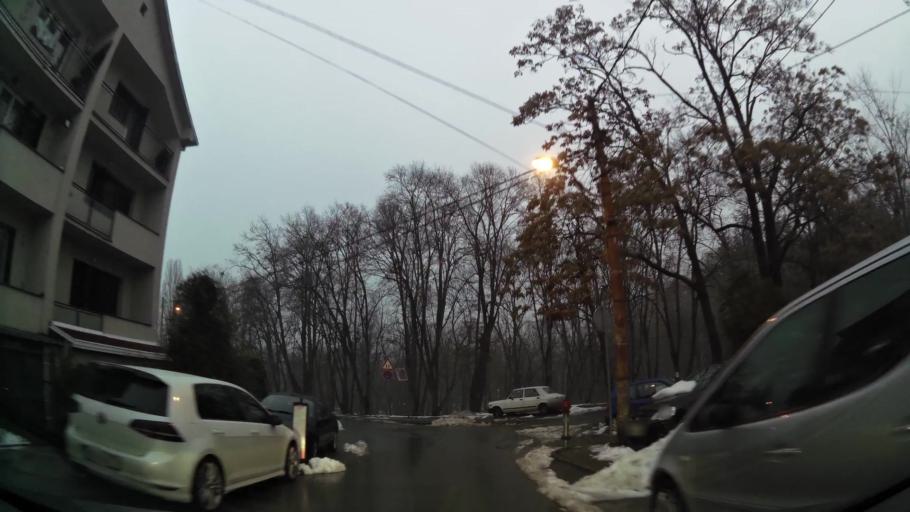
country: RS
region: Central Serbia
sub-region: Belgrade
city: Cukarica
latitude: 44.7630
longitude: 20.4220
